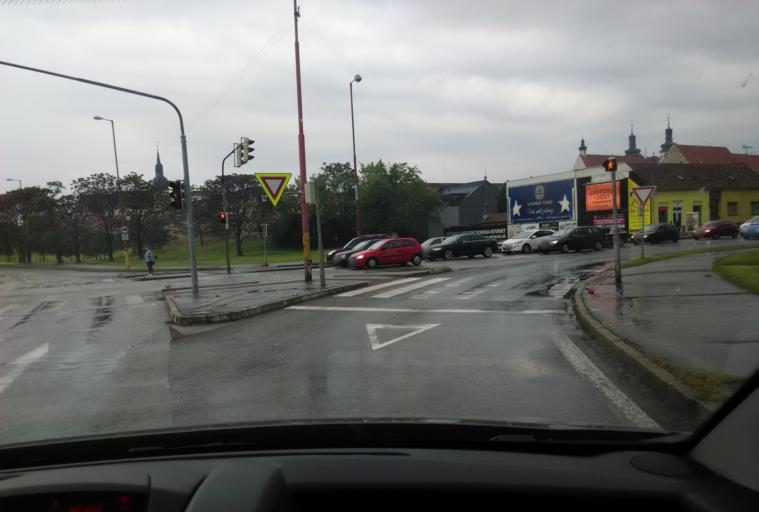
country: SK
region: Trnavsky
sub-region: Okres Trnava
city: Trnava
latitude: 48.3831
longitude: 17.5911
